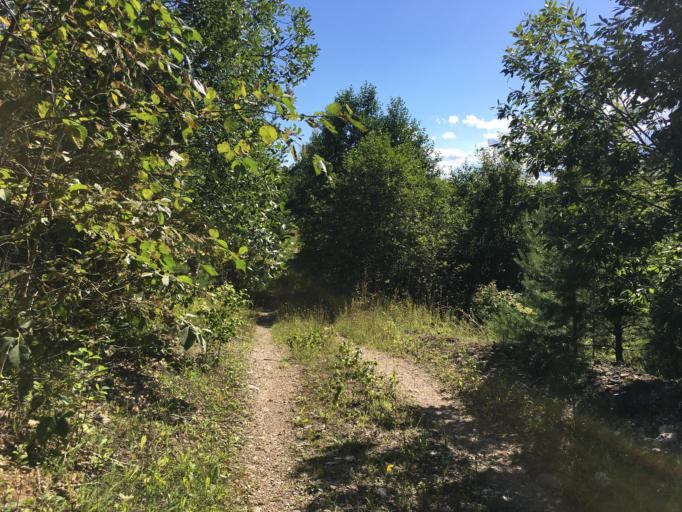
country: RU
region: Pskov
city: Izborsk
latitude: 57.8162
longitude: 27.9719
